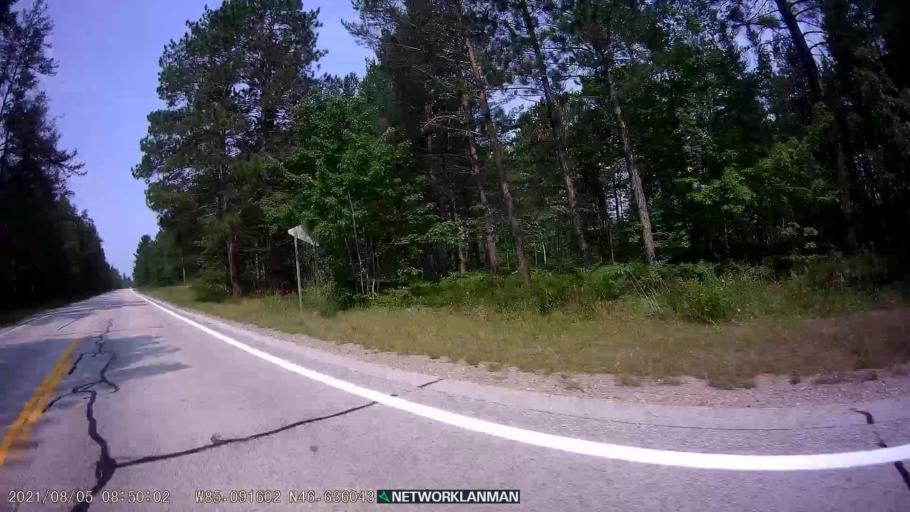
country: US
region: Michigan
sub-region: Luce County
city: Newberry
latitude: 46.6360
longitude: -85.0923
